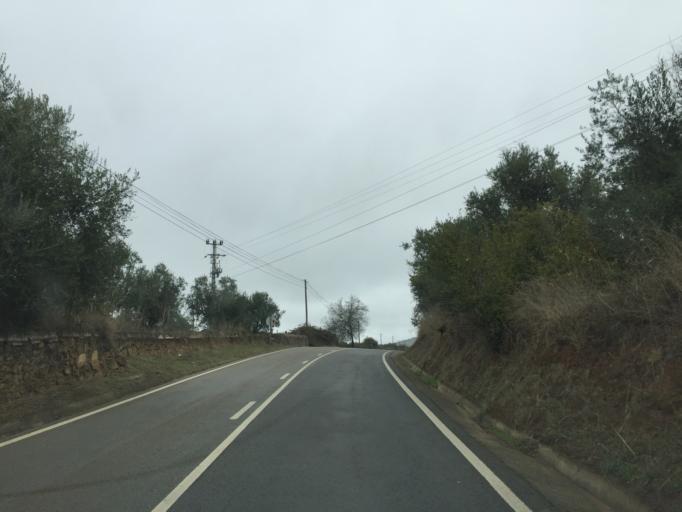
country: PT
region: Portalegre
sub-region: Alter do Chao
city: Alter do Chao
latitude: 39.2105
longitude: -7.6563
